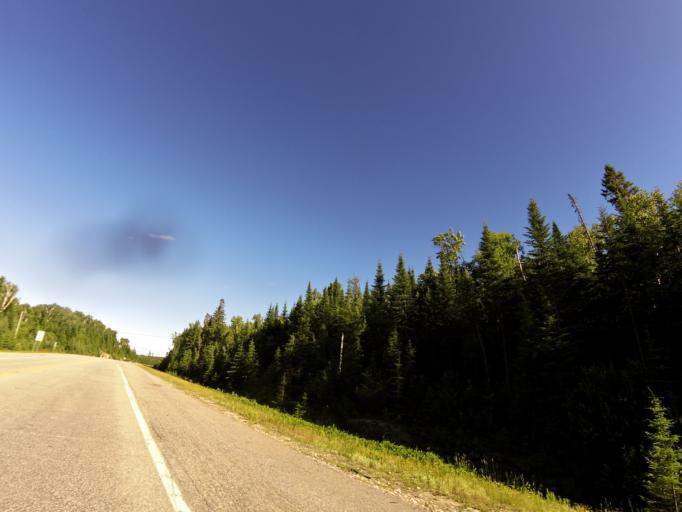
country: CA
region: Quebec
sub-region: Outaouais
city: Maniwaki
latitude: 47.1517
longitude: -76.6334
